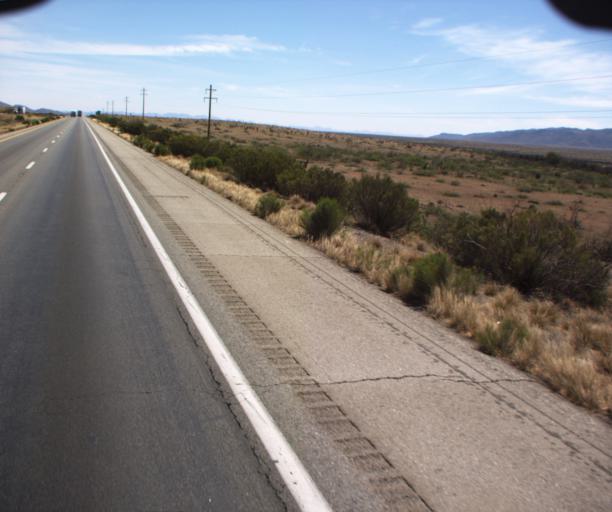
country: US
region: Arizona
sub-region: Cochise County
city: Willcox
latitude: 32.3512
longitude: -109.7275
